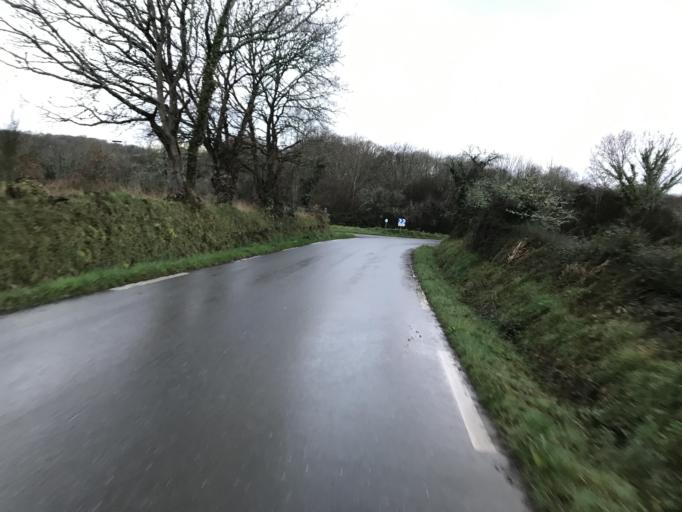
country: FR
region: Brittany
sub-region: Departement du Finistere
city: Plougastel-Daoulas
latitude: 48.3588
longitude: -4.3486
